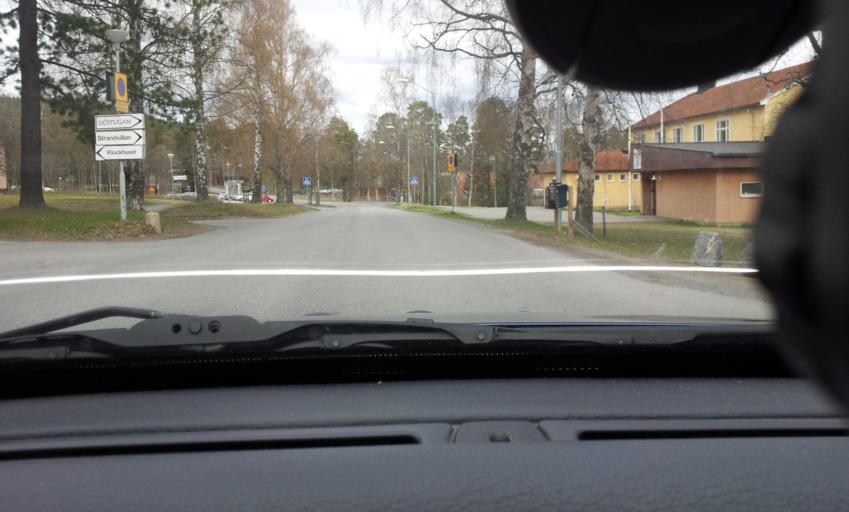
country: SE
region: Jaemtland
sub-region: OEstersunds Kommun
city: Ostersund
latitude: 63.1672
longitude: 14.6036
